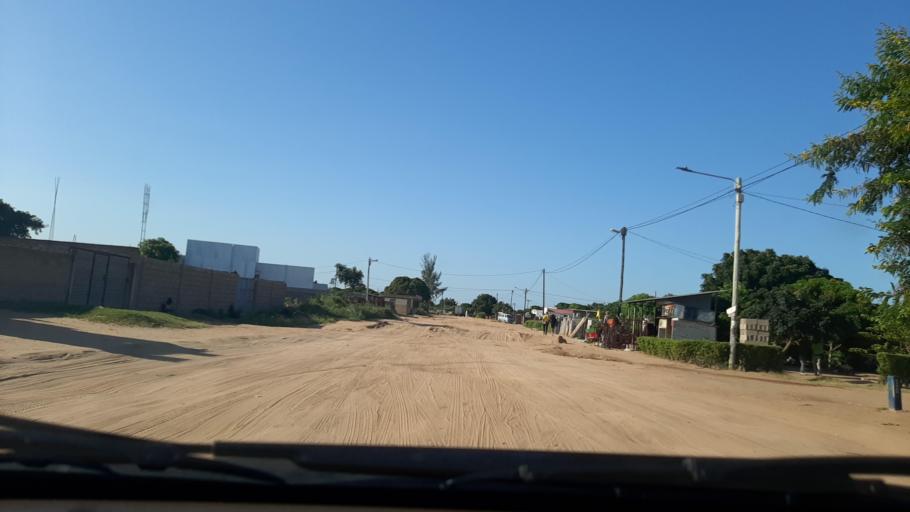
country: MZ
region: Maputo City
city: Maputo
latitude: -25.8058
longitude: 32.5467
